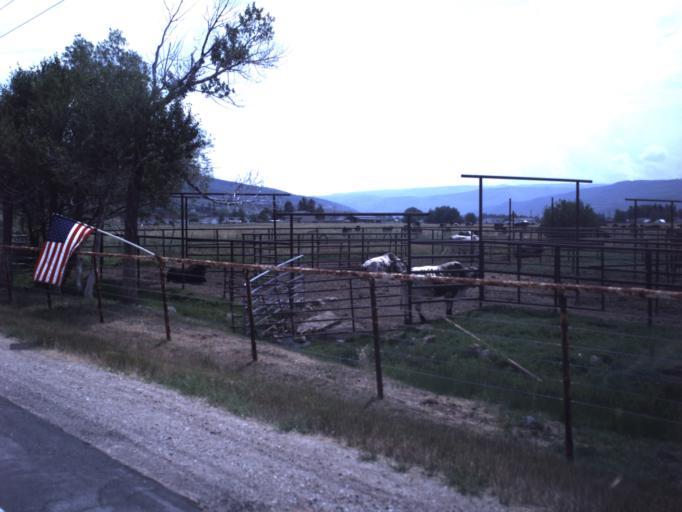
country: US
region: Utah
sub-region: Summit County
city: Francis
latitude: 40.6106
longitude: -111.2668
